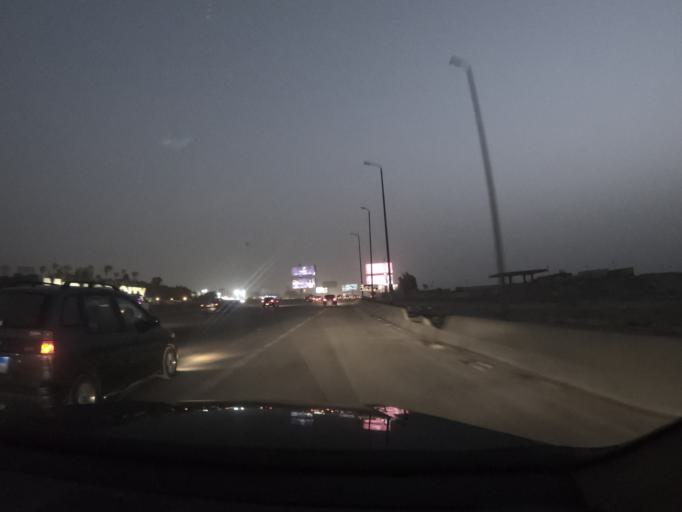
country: EG
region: Muhafazat al Qalyubiyah
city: Al Khankah
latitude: 30.0743
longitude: 31.4319
